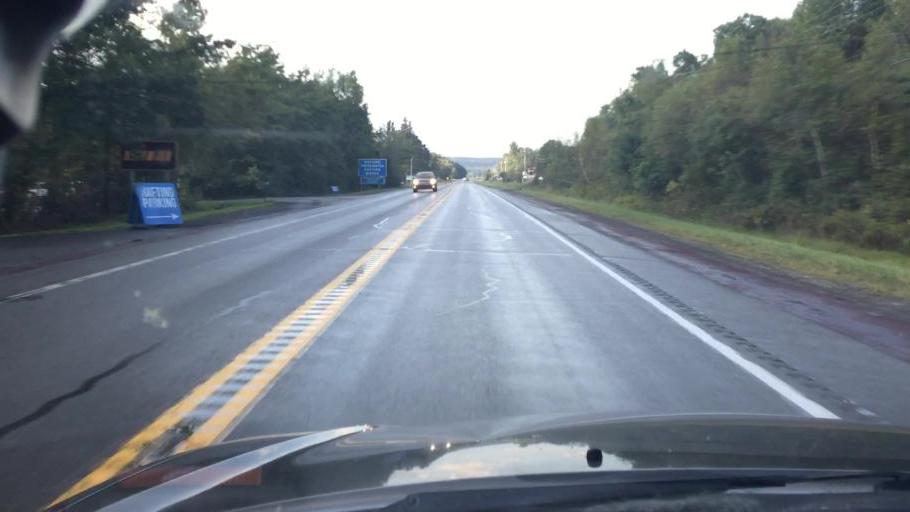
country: US
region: Pennsylvania
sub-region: Carbon County
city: Towamensing Trails
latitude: 40.9452
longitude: -75.6537
